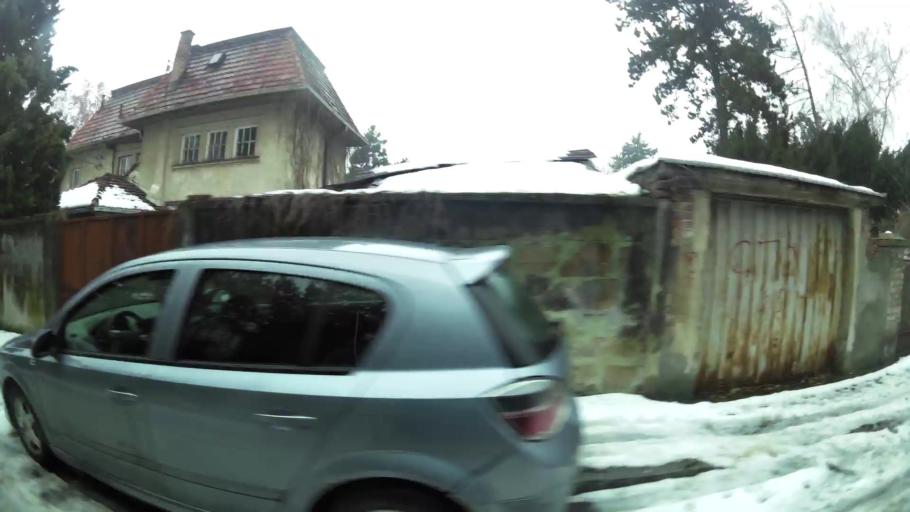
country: RS
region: Central Serbia
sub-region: Belgrade
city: Cukarica
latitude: 44.7922
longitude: 20.4309
